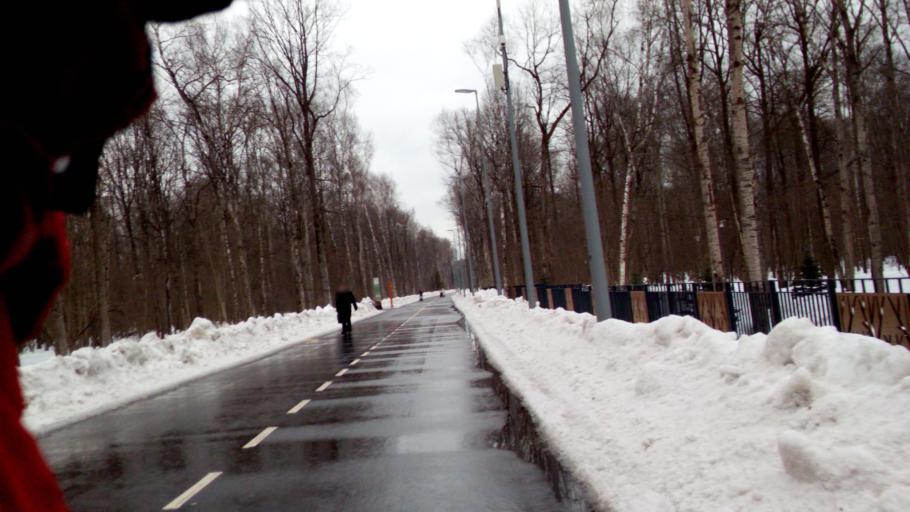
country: RU
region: Moskovskaya
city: Moskovskiy
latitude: 55.5986
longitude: 37.3765
